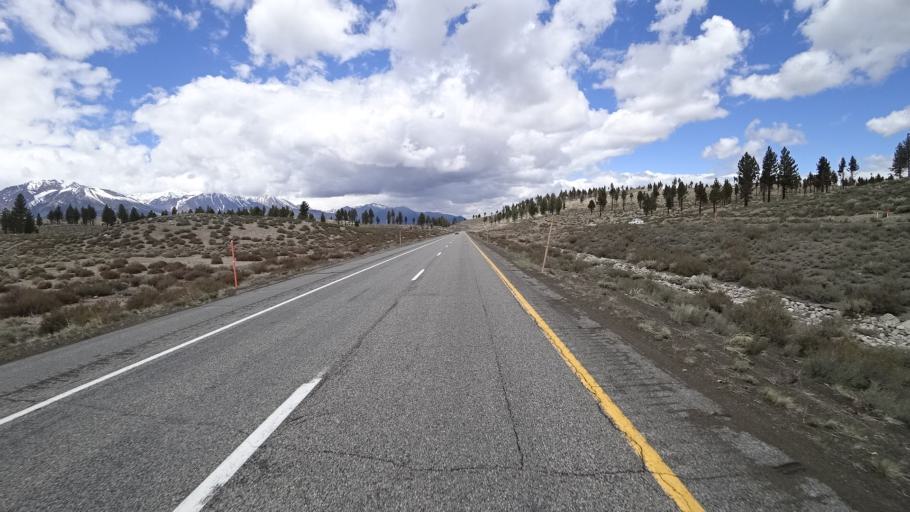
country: US
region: California
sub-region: Mono County
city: Mammoth Lakes
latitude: 37.8216
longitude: -119.0621
